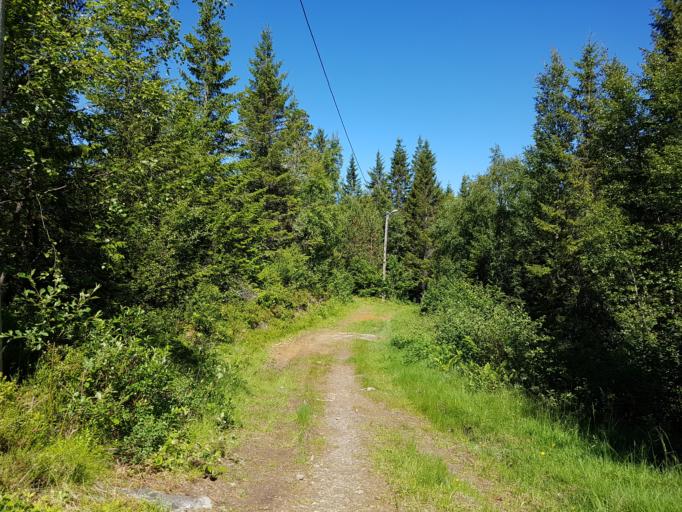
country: NO
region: Sor-Trondelag
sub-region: Skaun
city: Borsa
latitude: 63.4328
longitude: 10.1890
